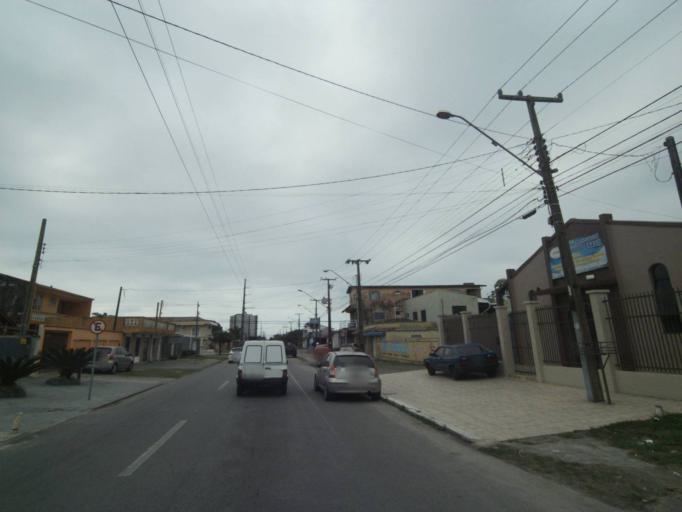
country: BR
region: Parana
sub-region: Paranagua
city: Paranagua
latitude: -25.5226
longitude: -48.5223
